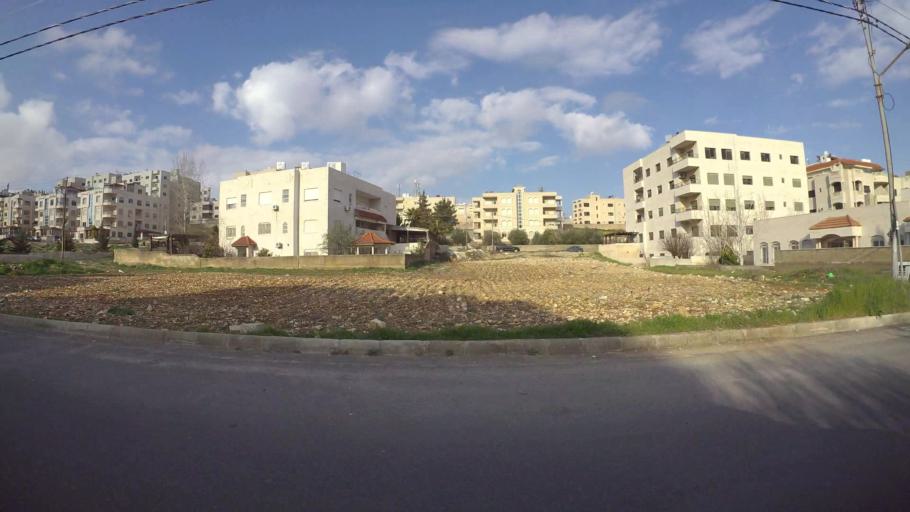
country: JO
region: Amman
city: Al Jubayhah
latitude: 31.9846
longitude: 35.8566
